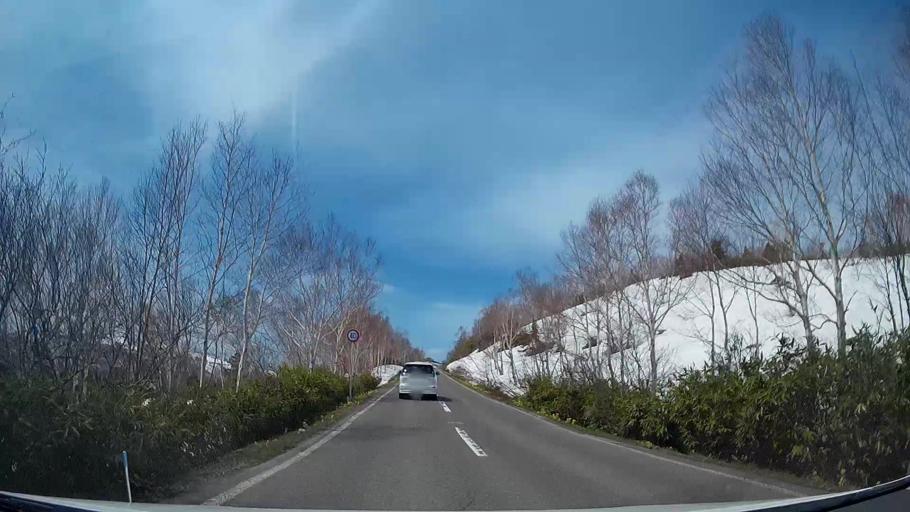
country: JP
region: Iwate
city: Shizukuishi
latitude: 39.9343
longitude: 140.9150
